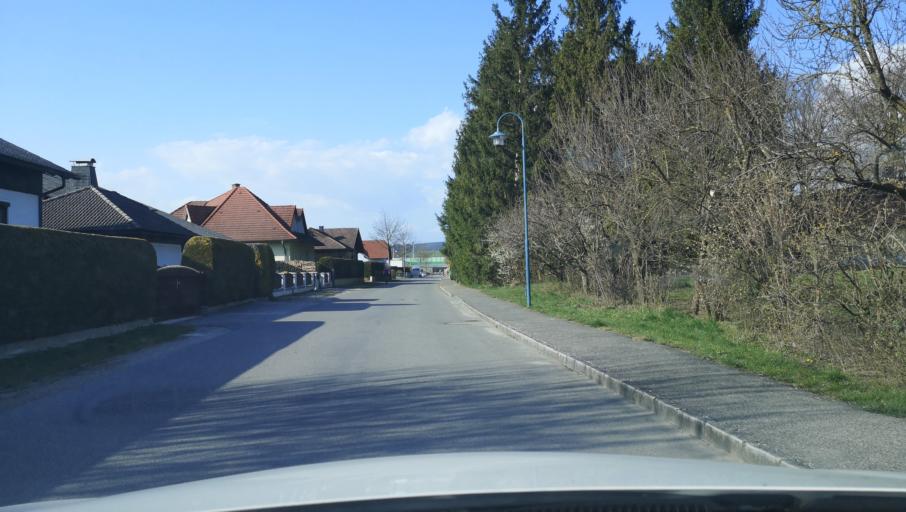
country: AT
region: Lower Austria
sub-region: Politischer Bezirk Melk
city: Blindenmarkt
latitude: 48.1223
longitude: 14.9880
